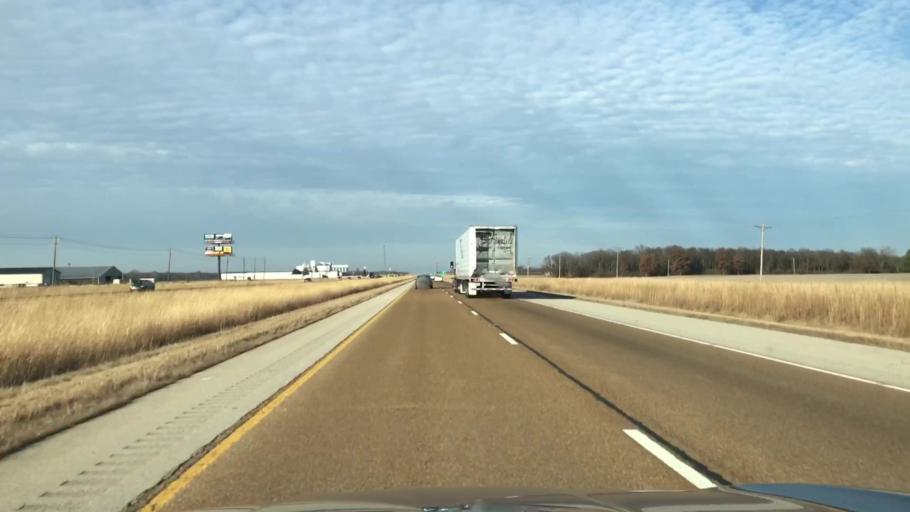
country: US
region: Illinois
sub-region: Montgomery County
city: Litchfield
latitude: 39.2599
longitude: -89.6410
